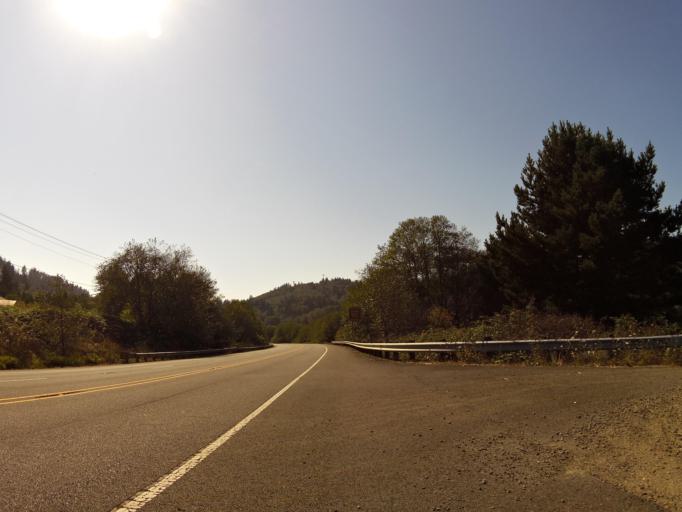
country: US
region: Oregon
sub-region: Tillamook County
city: Pacific City
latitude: 45.1586
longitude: -123.9485
